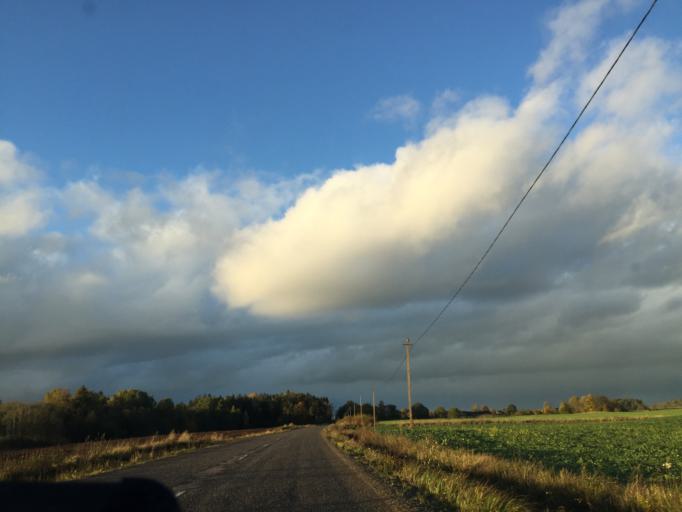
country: LV
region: Talsu Rajons
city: Sabile
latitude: 56.9008
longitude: 22.4008
